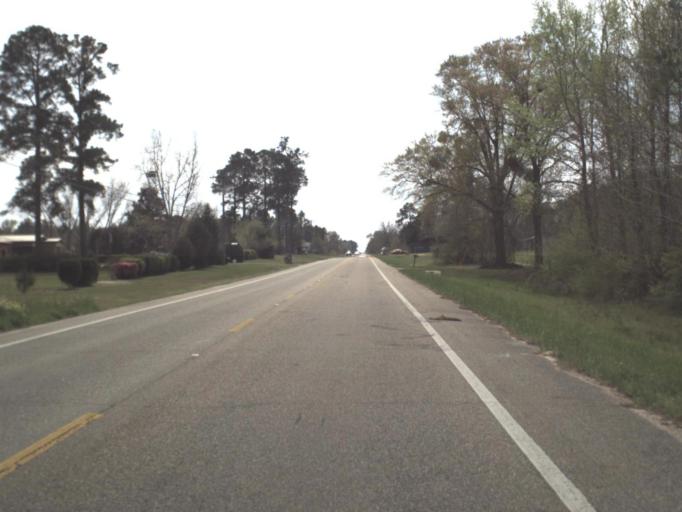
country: US
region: Florida
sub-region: Jackson County
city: Graceville
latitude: 30.8849
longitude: -85.5248
